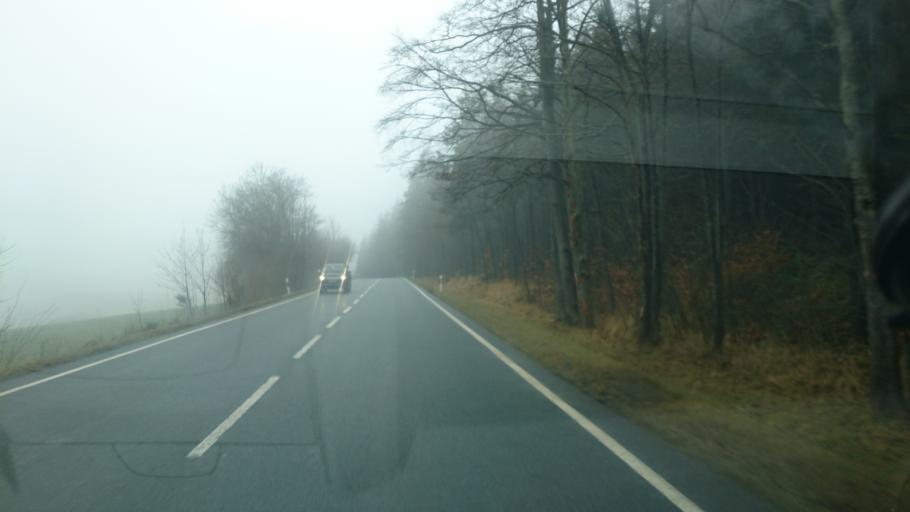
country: DE
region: Thuringia
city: Tanna
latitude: 50.4799
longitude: 11.8380
